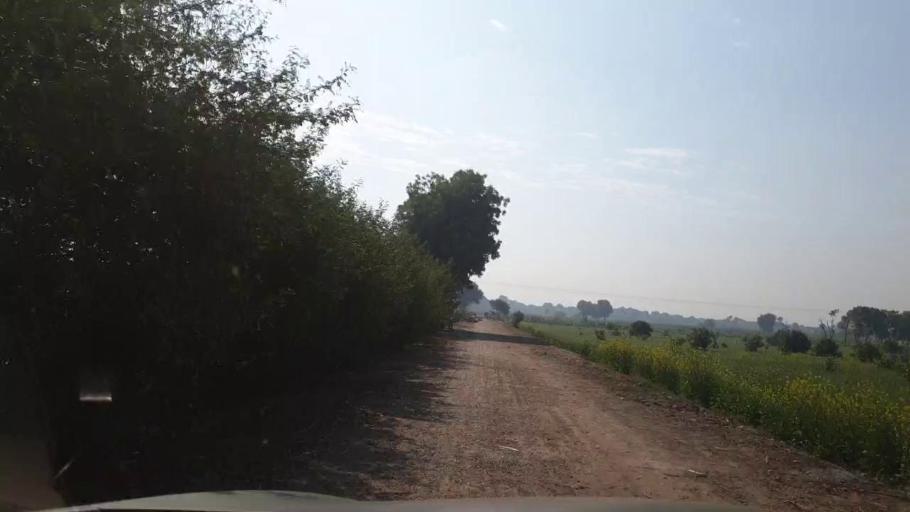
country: PK
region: Sindh
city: Tando Allahyar
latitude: 25.4623
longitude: 68.6575
